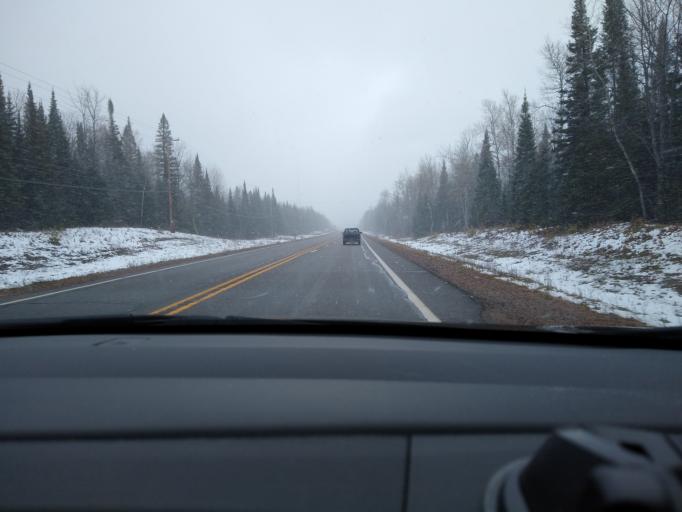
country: US
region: Wisconsin
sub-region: Florence County
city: Florence
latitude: 46.0522
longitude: -88.0631
